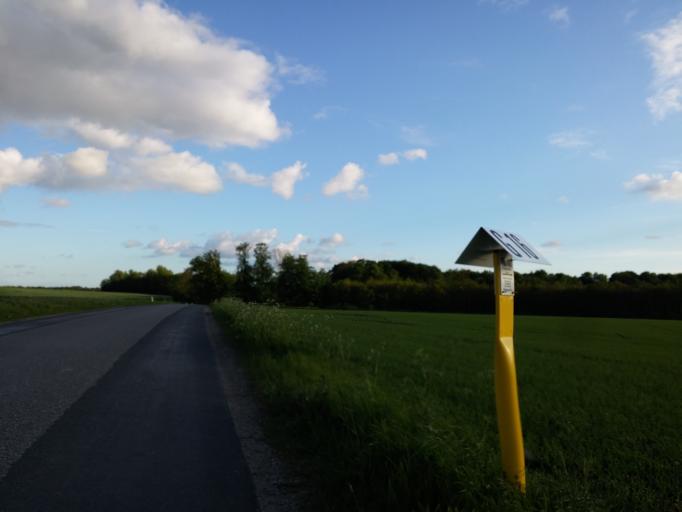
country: DK
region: South Denmark
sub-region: Kerteminde Kommune
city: Munkebo
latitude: 55.4316
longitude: 10.5397
